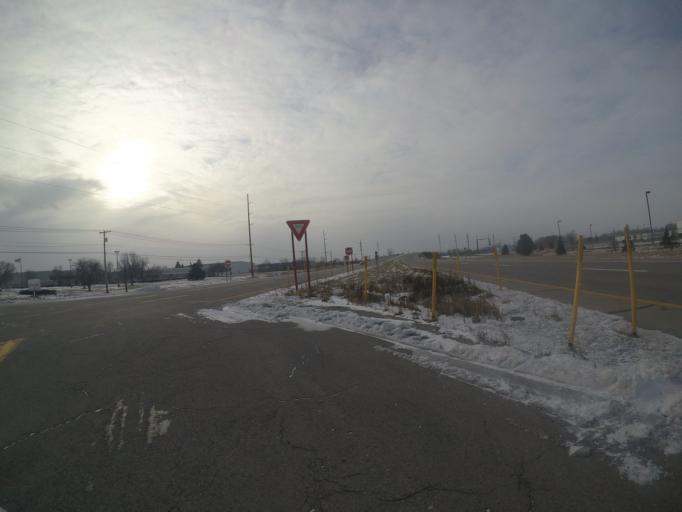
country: US
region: Ohio
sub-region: Wood County
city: Rossford
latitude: 41.5638
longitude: -83.5452
